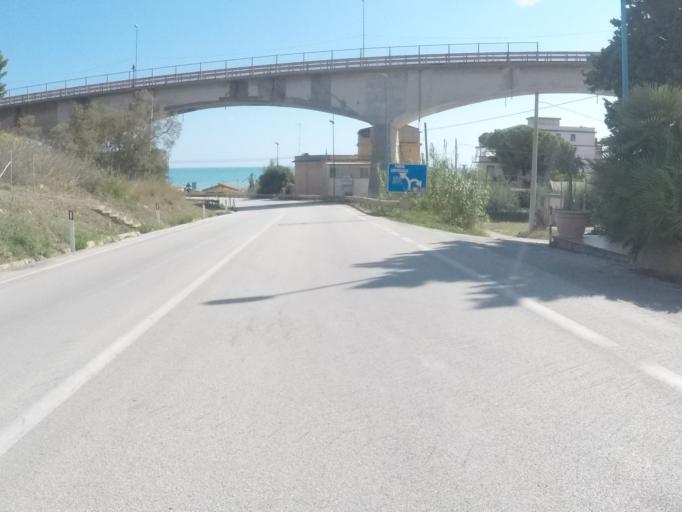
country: IT
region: Sicily
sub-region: Agrigento
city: Porto Empedocle
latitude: 37.2948
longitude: 13.5016
